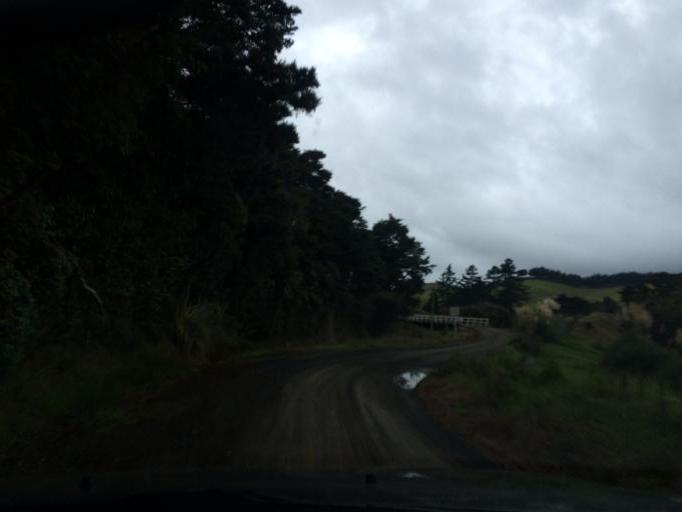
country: NZ
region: Northland
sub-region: Whangarei
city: Maungatapere
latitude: -35.8170
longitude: 174.0614
